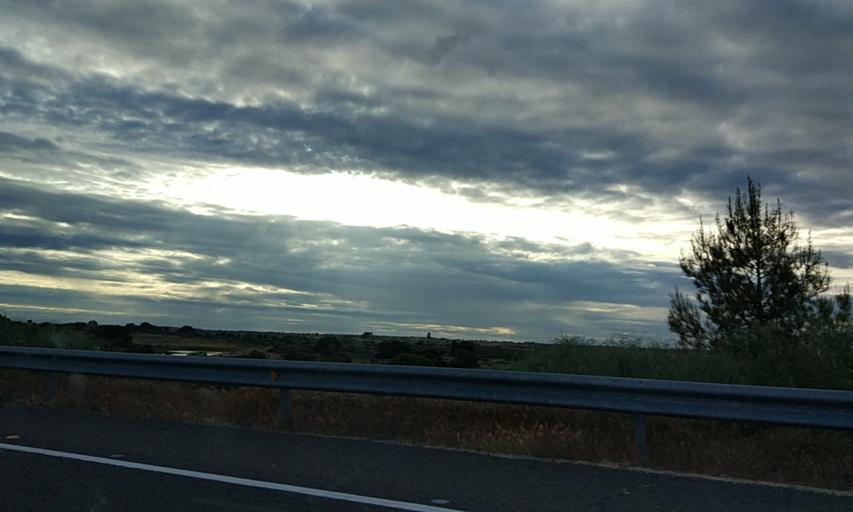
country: ES
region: Extremadura
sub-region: Provincia de Caceres
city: Casar de Caceres
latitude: 39.5115
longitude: -6.4318
